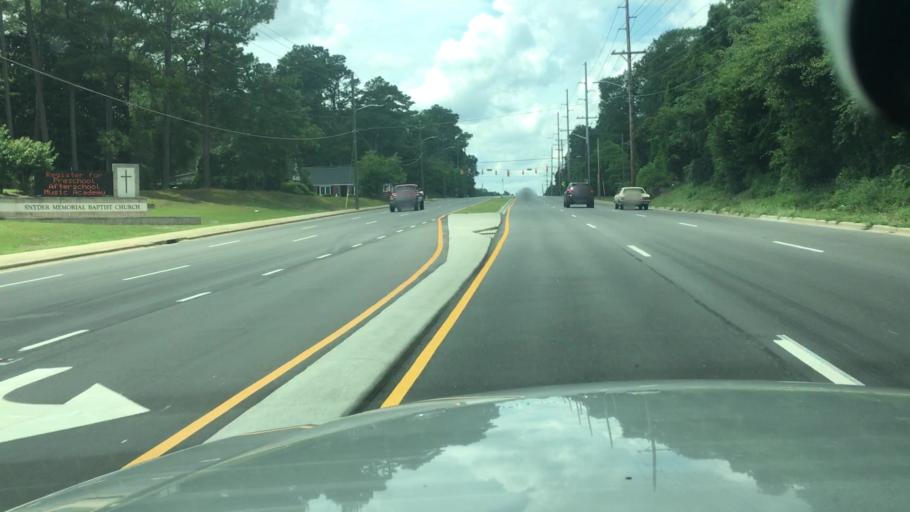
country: US
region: North Carolina
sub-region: Cumberland County
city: Fayetteville
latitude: 35.0685
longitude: -78.9054
